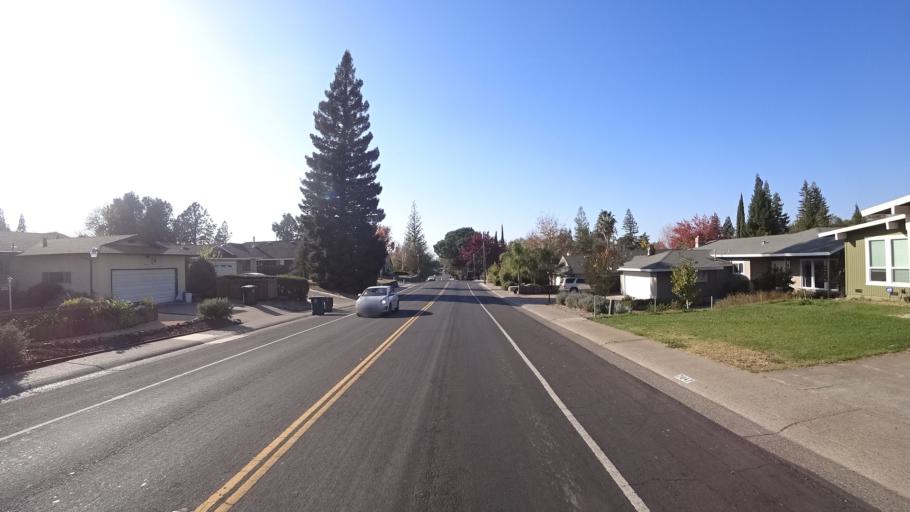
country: US
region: California
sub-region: Sacramento County
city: Fair Oaks
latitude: 38.6720
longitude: -121.2819
